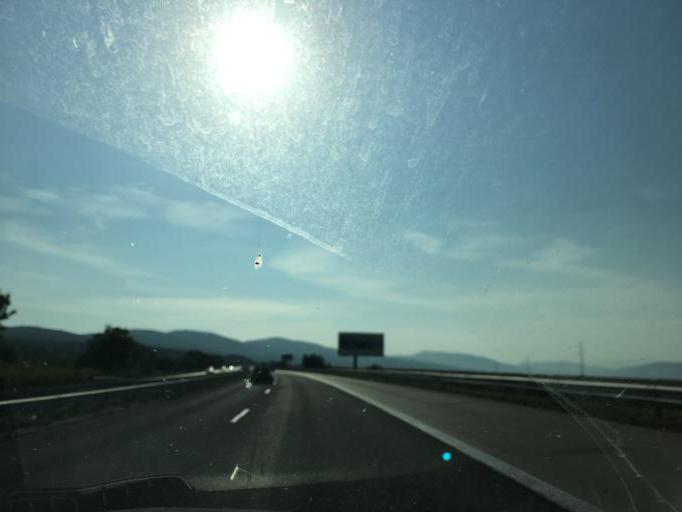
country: BG
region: Sofiya
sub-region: Obshtina Ikhtiman
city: Ikhtiman
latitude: 42.4772
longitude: 23.7978
